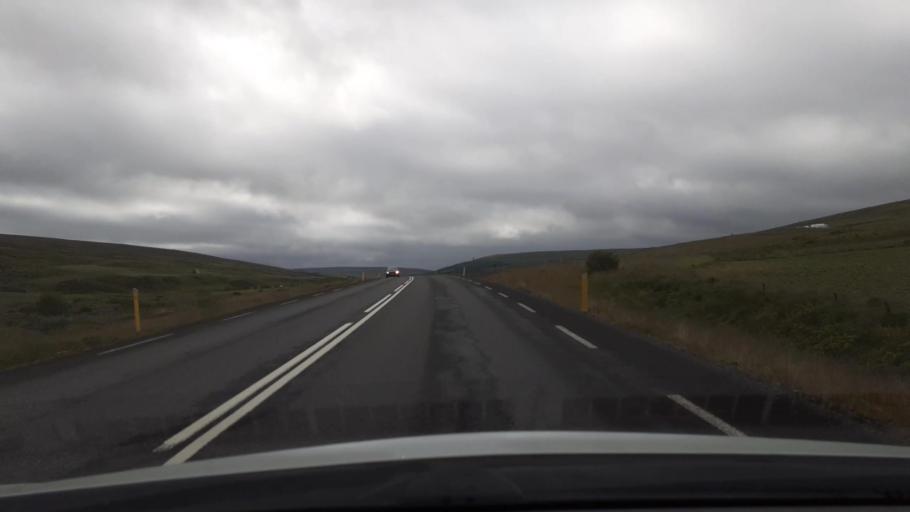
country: IS
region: Northeast
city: Laugar
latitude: 65.7027
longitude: -17.3587
